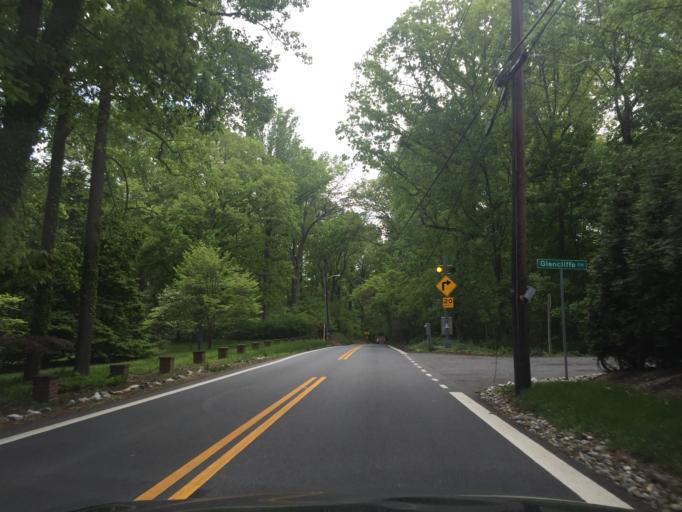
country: US
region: Maryland
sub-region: Baltimore County
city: Mays Chapel
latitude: 39.3965
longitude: -76.6773
